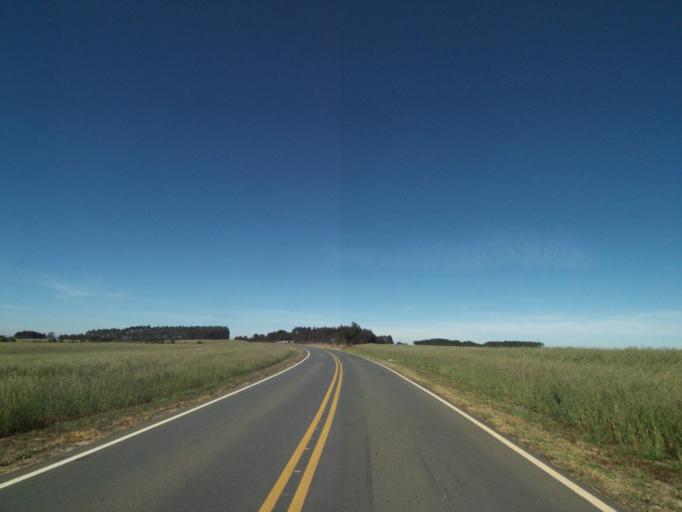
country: BR
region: Parana
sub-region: Castro
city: Castro
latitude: -24.7104
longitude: -50.1942
